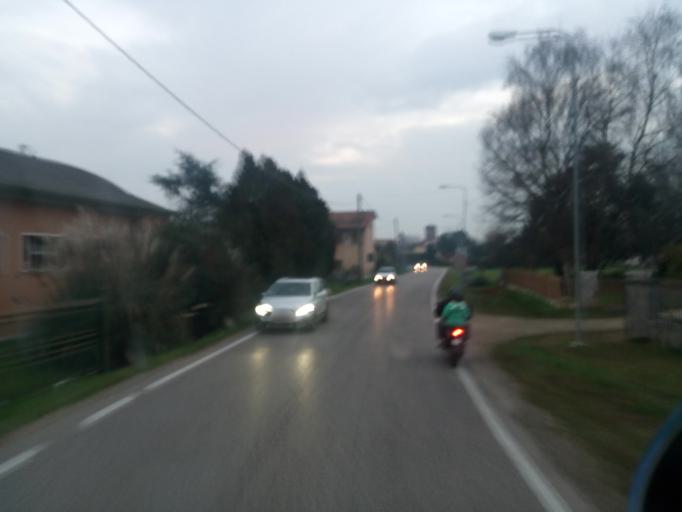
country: IT
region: Lombardy
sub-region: Provincia di Mantova
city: Roncoferraro
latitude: 45.1407
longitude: 10.9387
